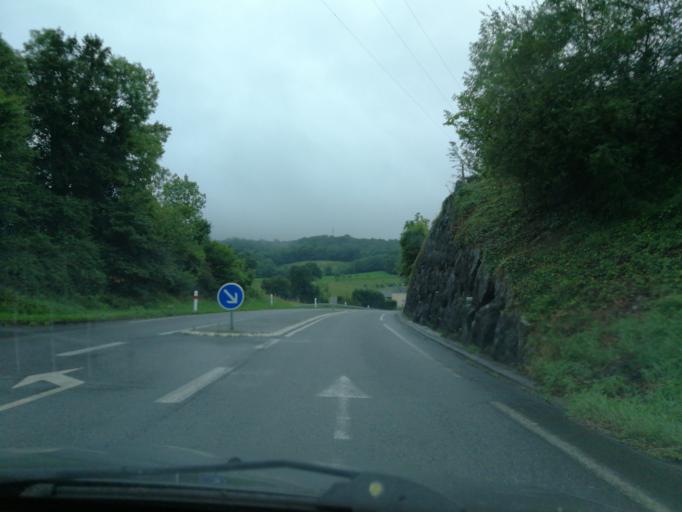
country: FR
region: Aquitaine
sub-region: Departement des Pyrenees-Atlantiques
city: Arudy
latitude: 43.1706
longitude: -0.4415
